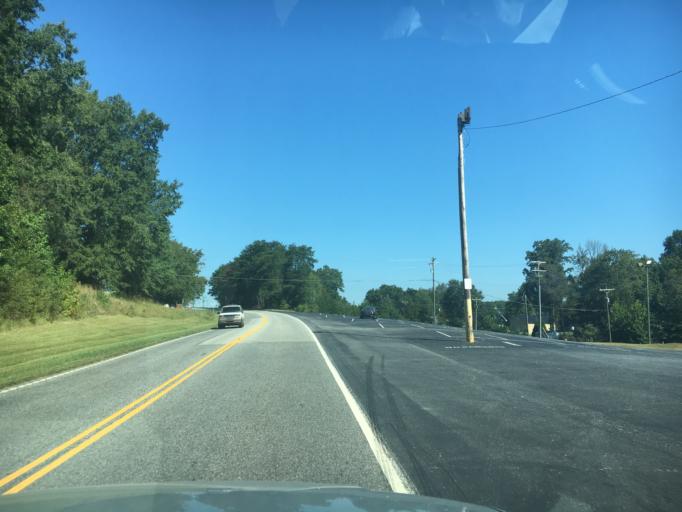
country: US
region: South Carolina
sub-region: Spartanburg County
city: Inman
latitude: 35.1151
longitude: -82.0407
